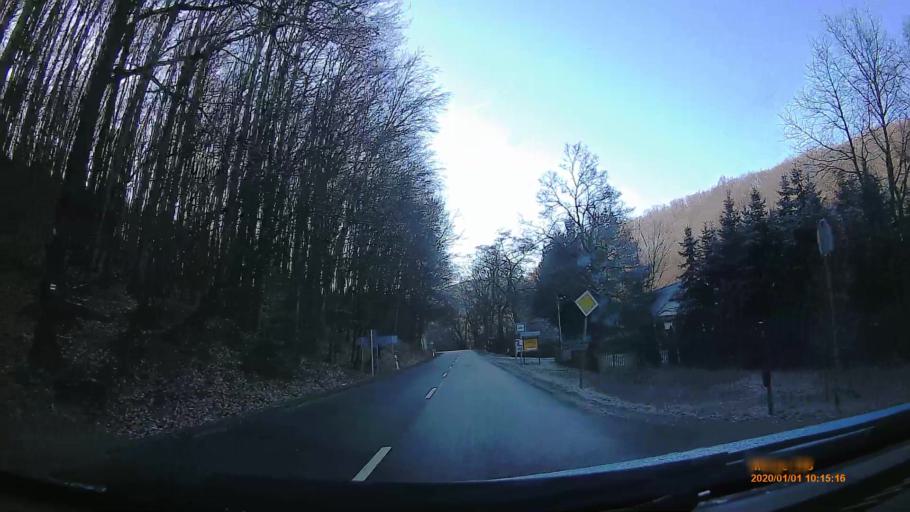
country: HU
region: Heves
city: Paradsasvar
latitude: 47.9179
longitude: 19.9945
